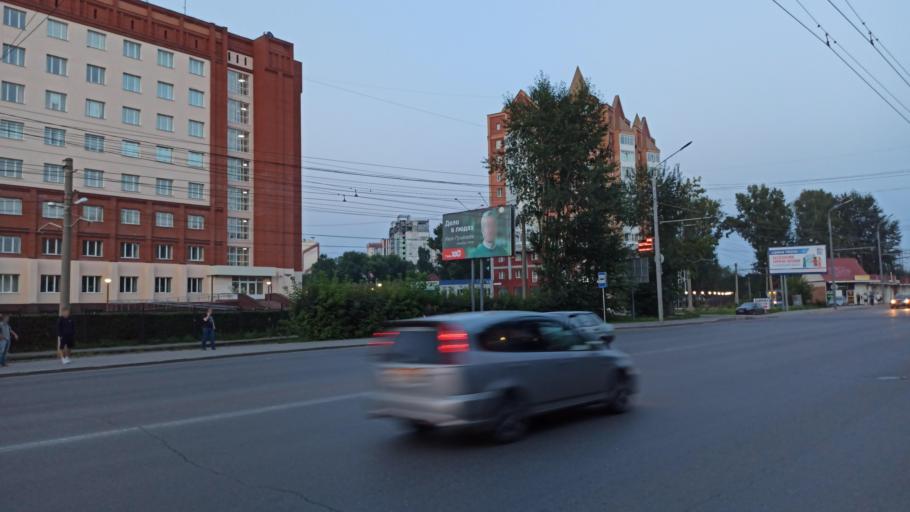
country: RU
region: Tomsk
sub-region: Tomskiy Rayon
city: Tomsk
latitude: 56.4539
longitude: 84.9768
